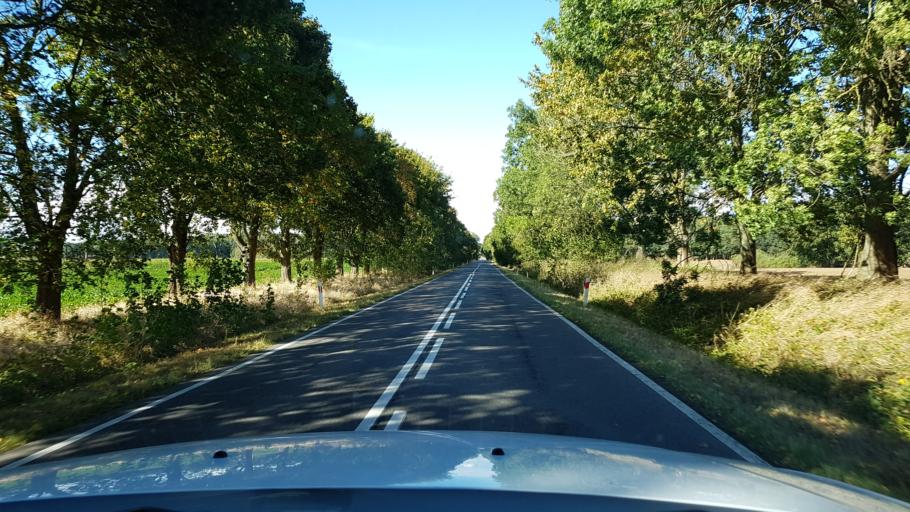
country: PL
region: West Pomeranian Voivodeship
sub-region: Powiat gryfinski
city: Banie
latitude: 53.1555
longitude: 14.6038
